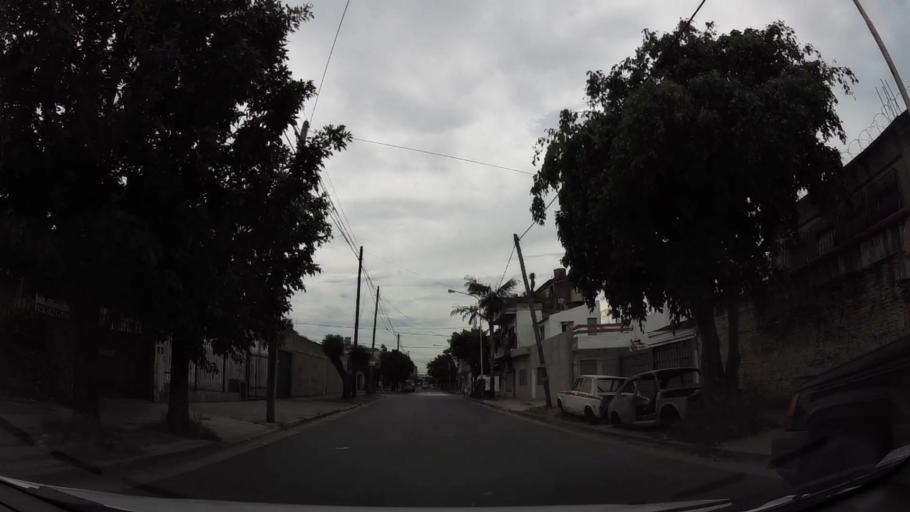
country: AR
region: Buenos Aires F.D.
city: Villa Lugano
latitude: -34.6708
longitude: -58.5114
